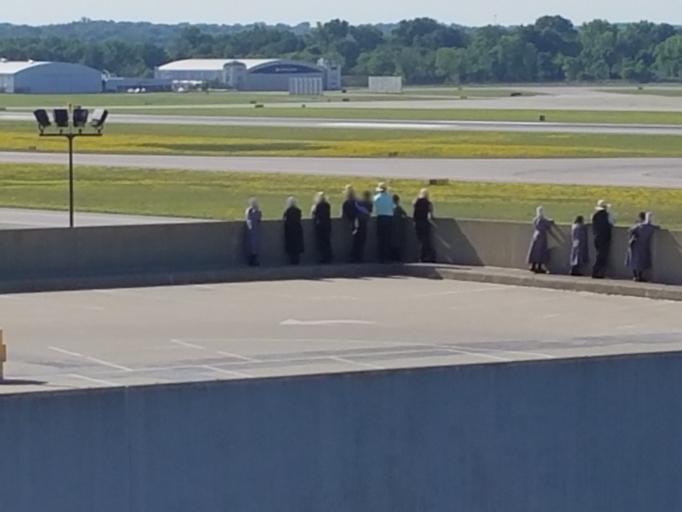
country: US
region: Ohio
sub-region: Franklin County
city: Whitehall
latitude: 39.9881
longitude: -82.8733
